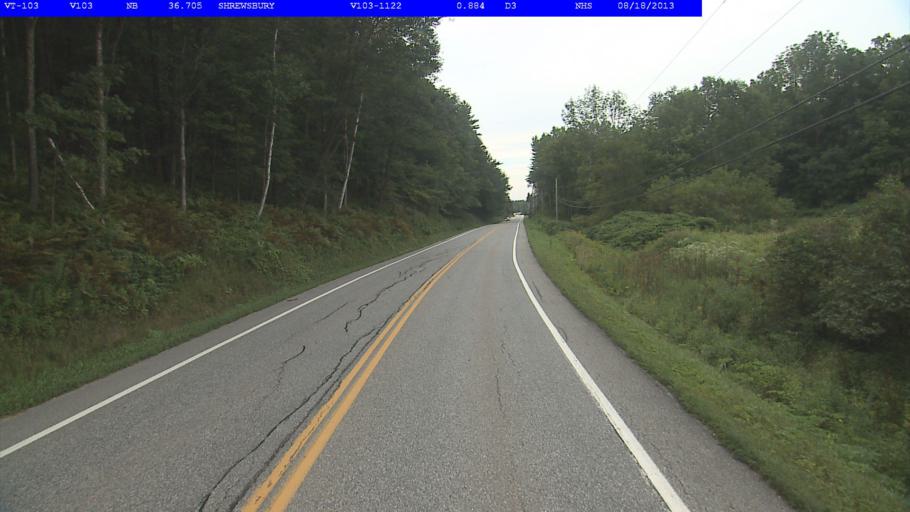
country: US
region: Vermont
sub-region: Rutland County
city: Rutland
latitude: 43.4852
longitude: -72.8967
